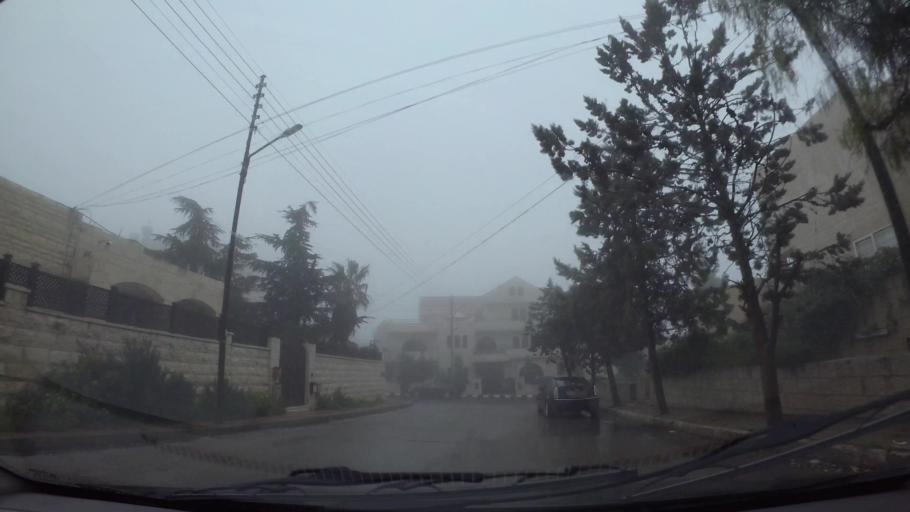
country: JO
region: Amman
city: Al Jubayhah
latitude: 32.0106
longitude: 35.8811
